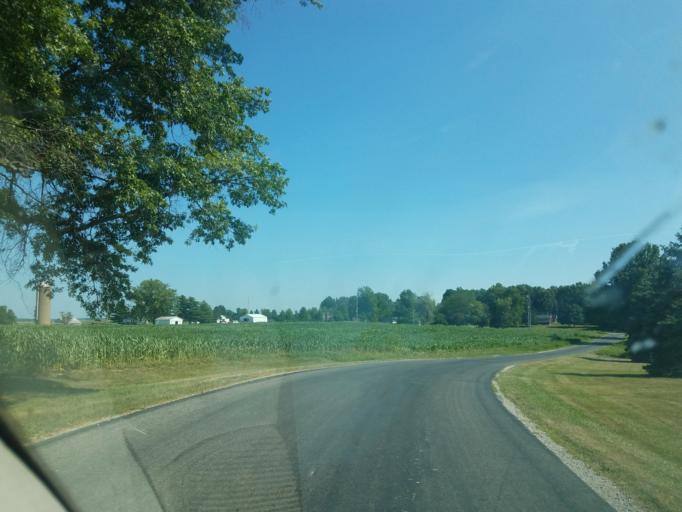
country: US
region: Ohio
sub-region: Crawford County
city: Bucyrus
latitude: 40.8004
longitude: -82.9306
